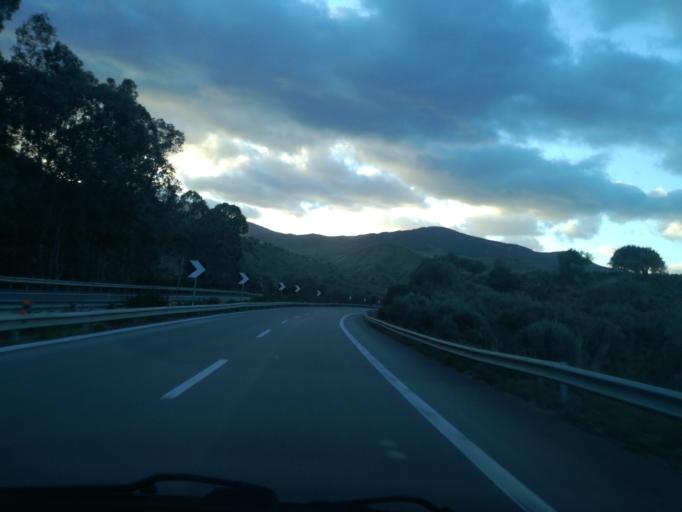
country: IT
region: Sicily
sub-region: Palermo
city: Scillato
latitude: 37.8635
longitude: 13.8817
